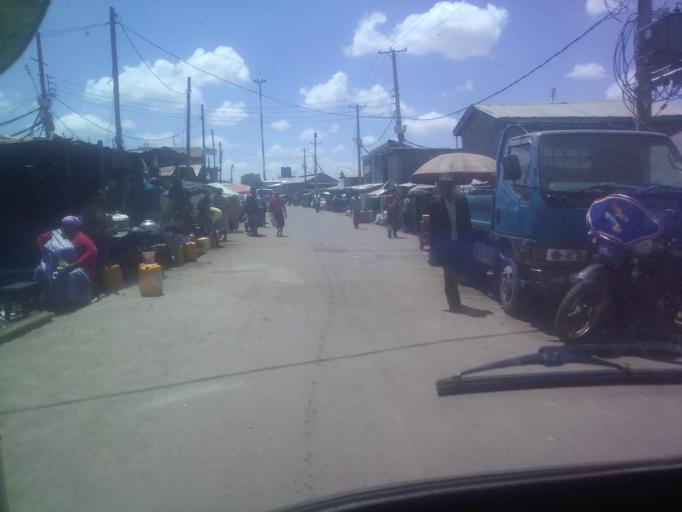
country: KE
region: Nairobi Area
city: Nairobi
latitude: -1.3120
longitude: 36.7940
